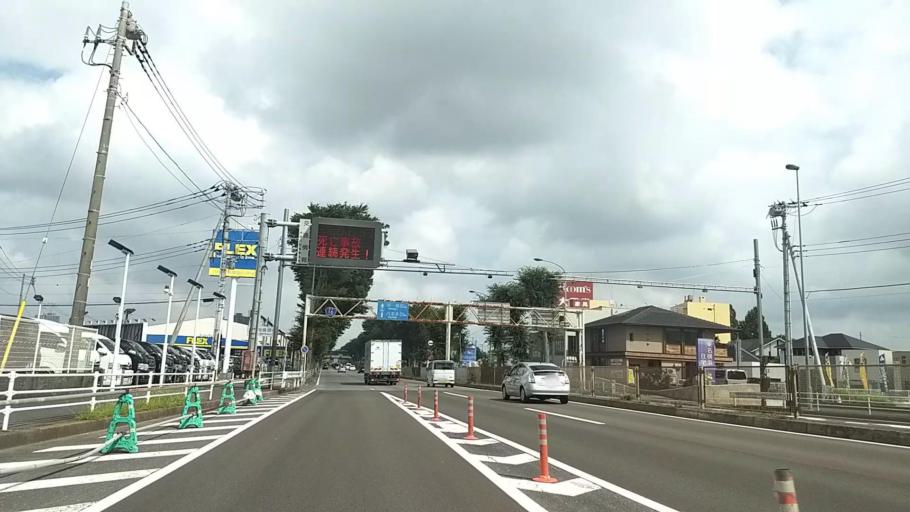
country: JP
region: Tokyo
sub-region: Machida-shi
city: Machida
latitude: 35.5185
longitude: 139.4538
